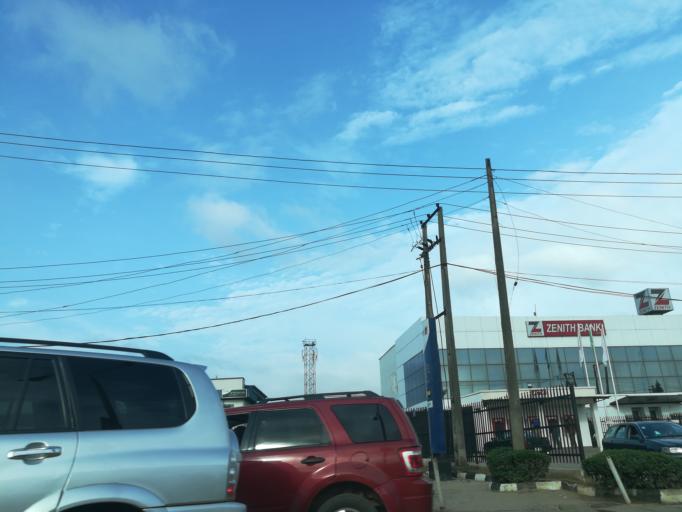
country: NG
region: Lagos
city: Ebute Ikorodu
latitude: 6.6050
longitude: 3.4852
